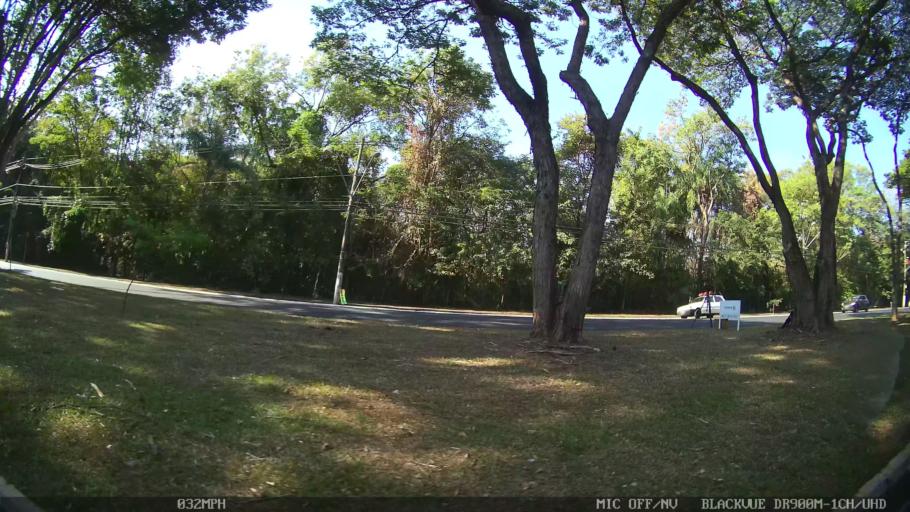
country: BR
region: Sao Paulo
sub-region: Ribeirao Preto
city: Ribeirao Preto
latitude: -21.1970
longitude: -47.7946
